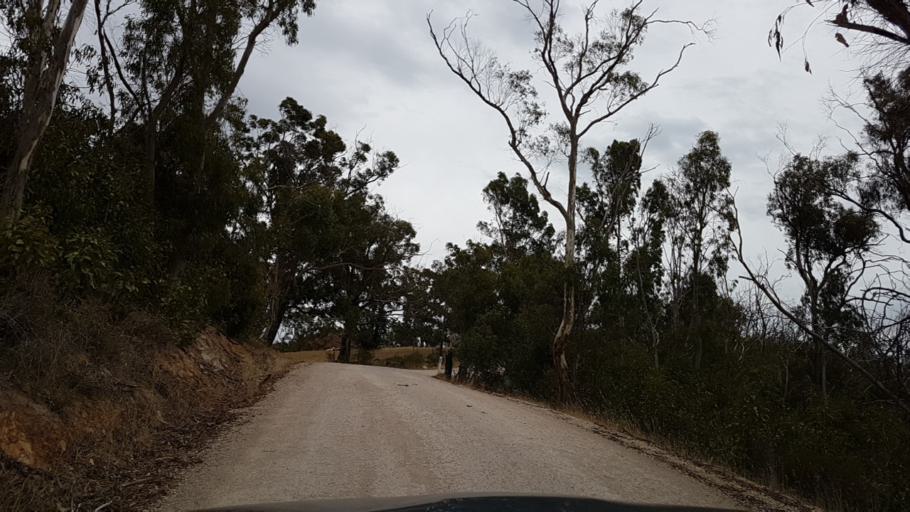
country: AU
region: South Australia
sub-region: Adelaide Hills
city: Gumeracha
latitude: -34.7896
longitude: 138.8131
